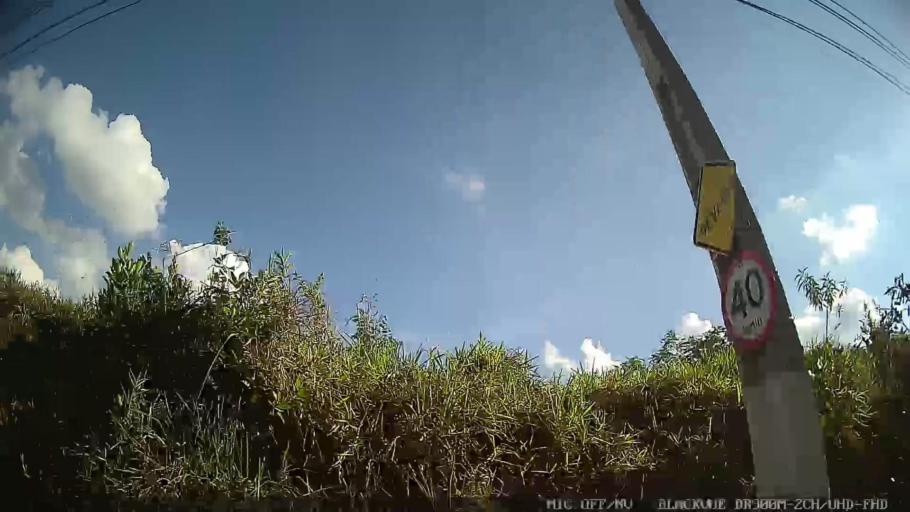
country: BR
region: Sao Paulo
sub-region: Braganca Paulista
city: Braganca Paulista
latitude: -22.9661
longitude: -46.5150
